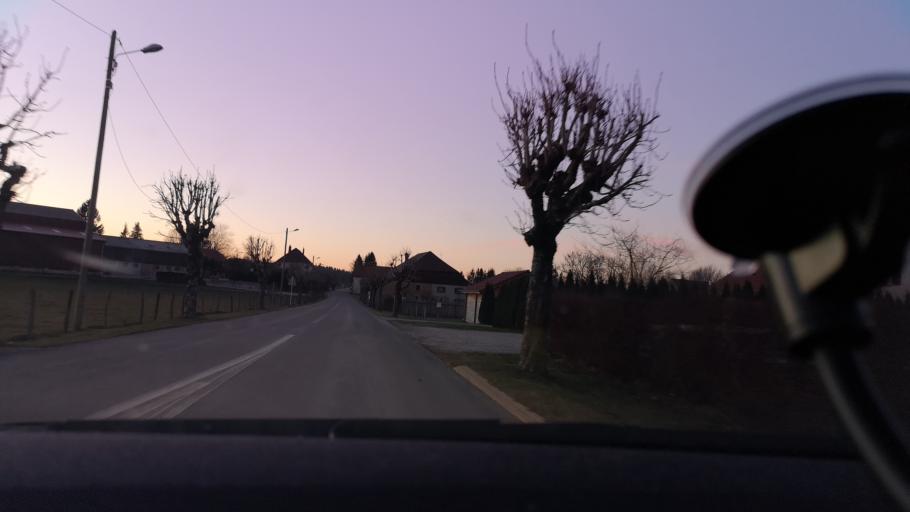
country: FR
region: Franche-Comte
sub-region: Departement du Doubs
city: Frasne
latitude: 46.8155
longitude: 6.0632
